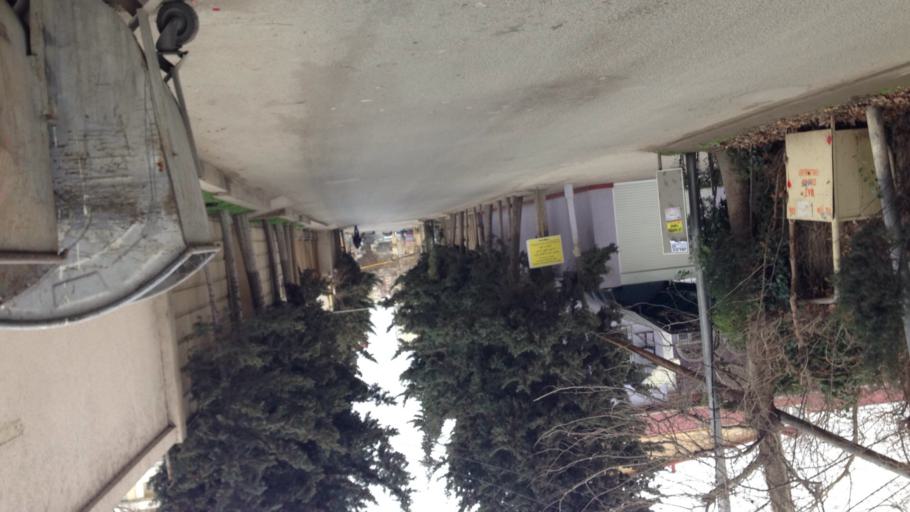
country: AZ
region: Baki
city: Bilajari
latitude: 40.4079
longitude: 49.8451
